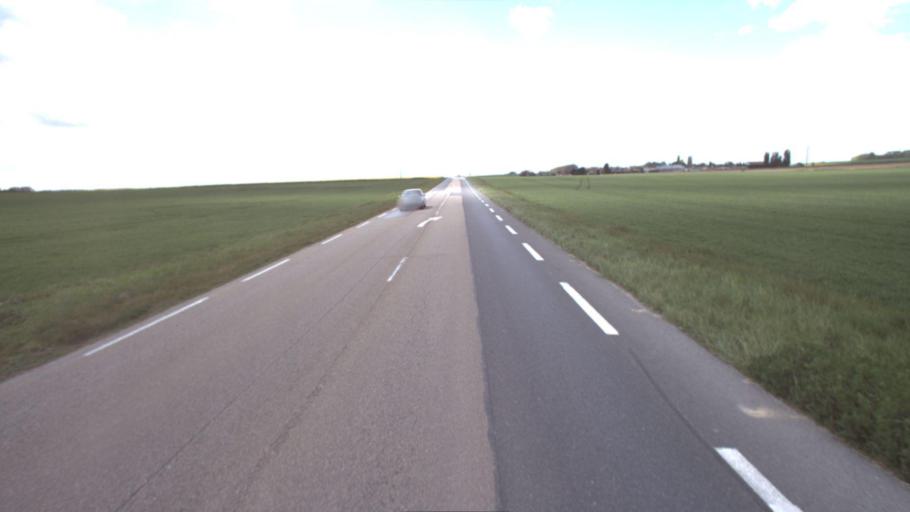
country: FR
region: Ile-de-France
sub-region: Departement de Seine-et-Marne
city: Villiers-Saint-Georges
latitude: 48.6913
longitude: 3.3547
